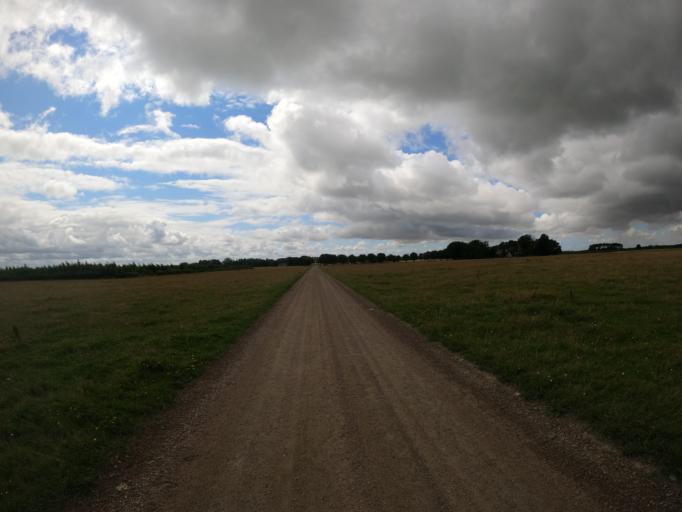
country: SE
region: Skane
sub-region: Hoors Kommun
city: Loberod
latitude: 55.7235
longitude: 13.4464
